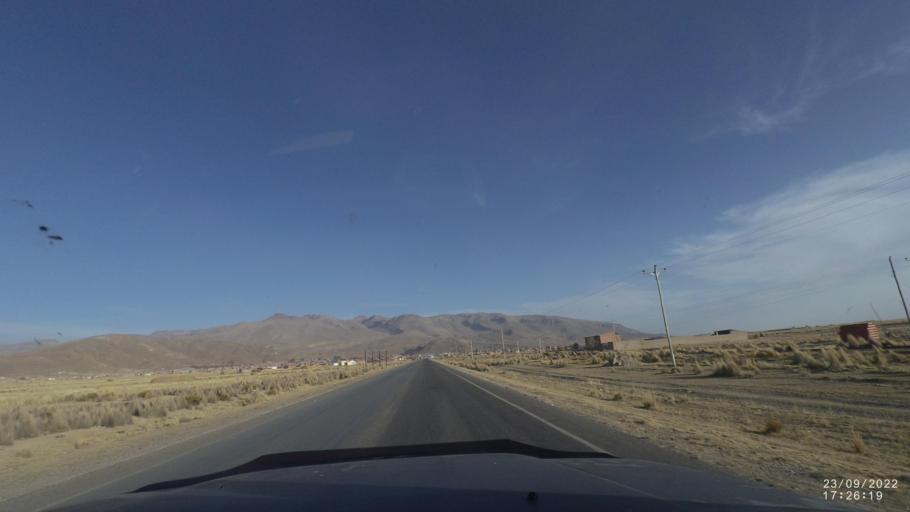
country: BO
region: Oruro
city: Challapata
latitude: -18.8833
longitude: -66.7870
